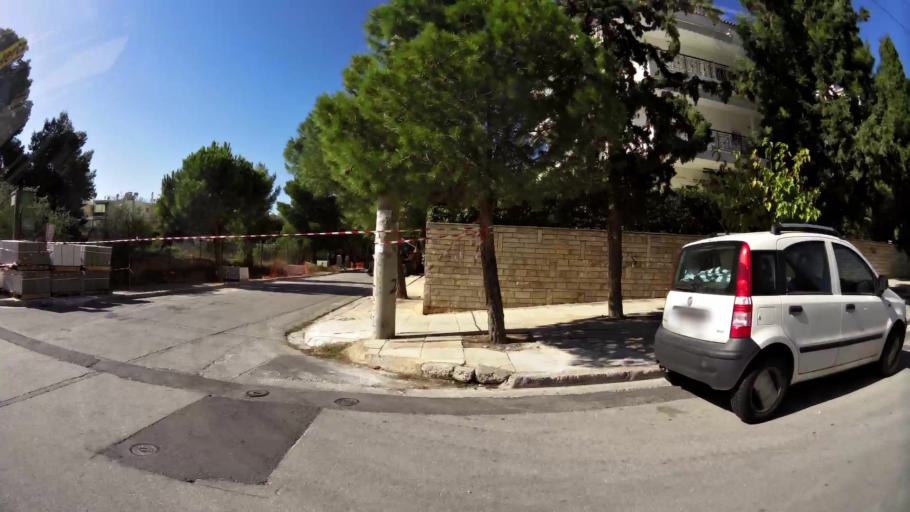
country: GR
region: Attica
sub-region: Nomarchia Anatolikis Attikis
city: Vouliagmeni
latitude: 37.8171
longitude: 23.7813
